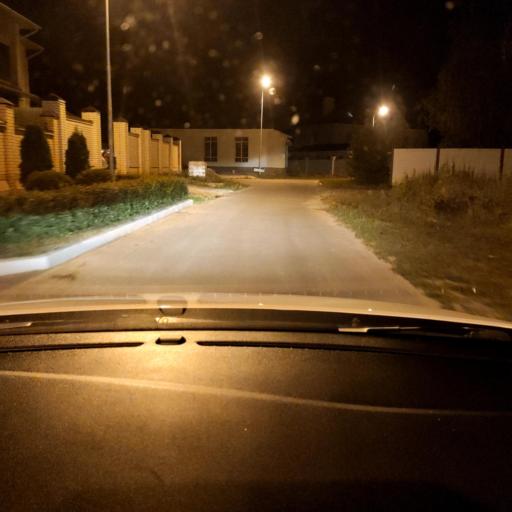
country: RU
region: Tatarstan
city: Osinovo
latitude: 55.8595
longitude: 48.7937
